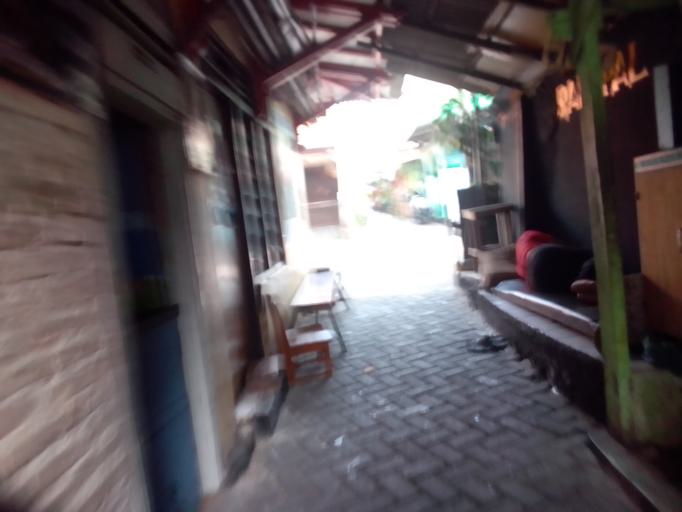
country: ID
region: Jakarta Raya
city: Jakarta
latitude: -6.1984
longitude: 106.8158
